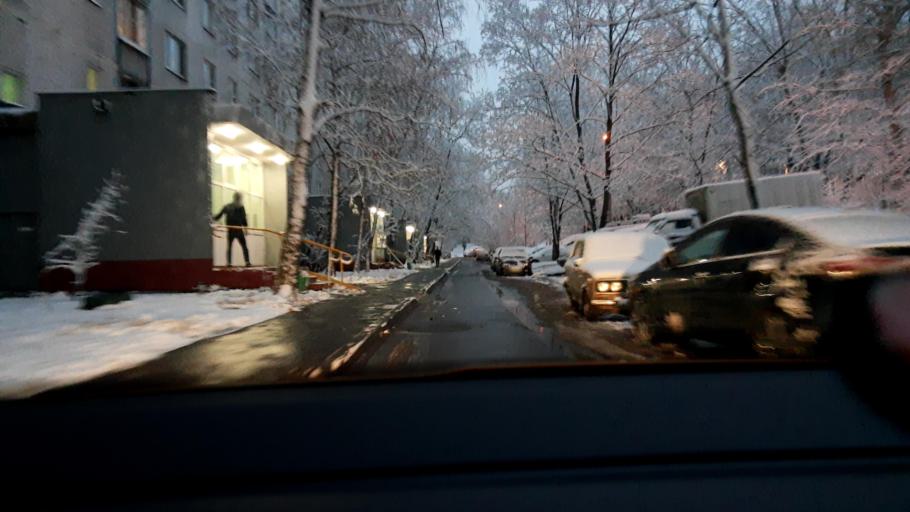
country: RU
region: Moscow
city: Lyublino
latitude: 55.6793
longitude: 37.7754
